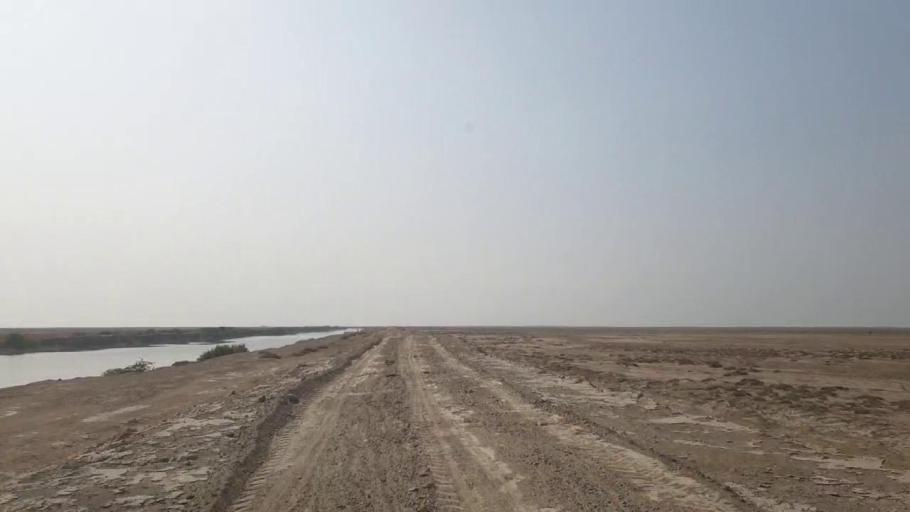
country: PK
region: Sindh
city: Kadhan
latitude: 24.3402
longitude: 68.8587
